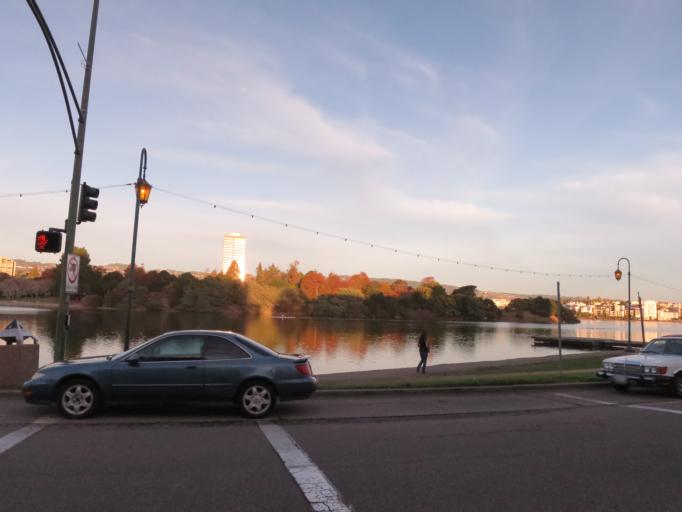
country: US
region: California
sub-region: Alameda County
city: Oakland
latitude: 37.8052
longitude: -122.2622
